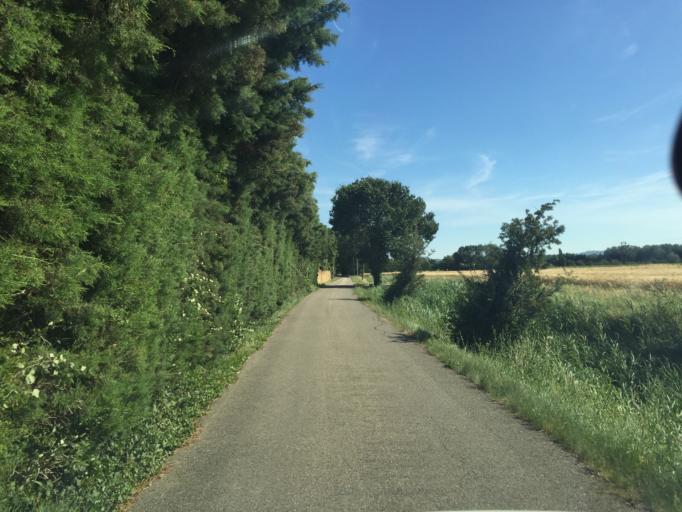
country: FR
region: Provence-Alpes-Cote d'Azur
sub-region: Departement du Vaucluse
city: Caderousse
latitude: 44.1080
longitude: 4.7422
